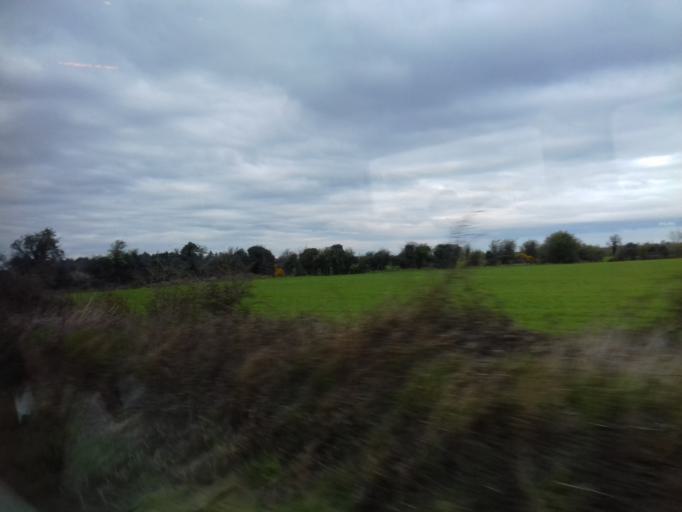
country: IE
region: Leinster
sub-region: An Longfort
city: Granard
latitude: 53.6730
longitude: -7.5164
